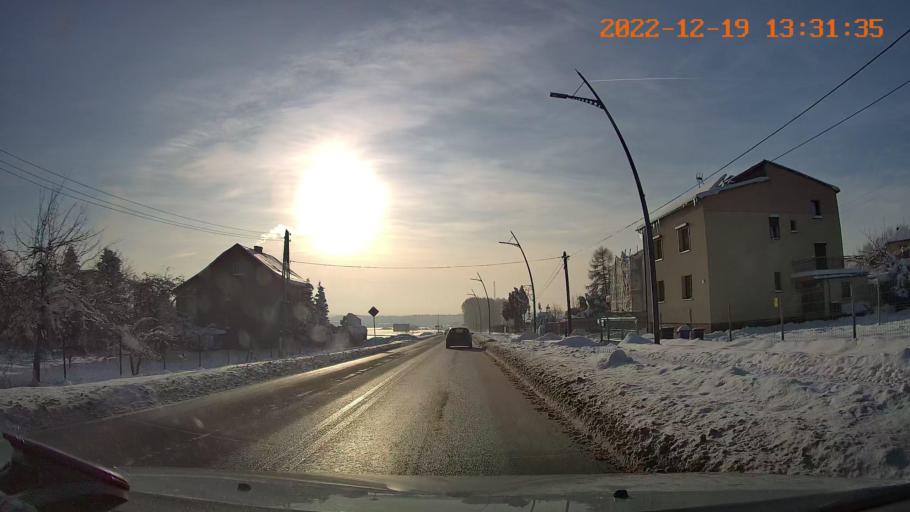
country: PL
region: Silesian Voivodeship
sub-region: Powiat bierunsko-ledzinski
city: Bierun
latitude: 50.1174
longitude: 19.1073
